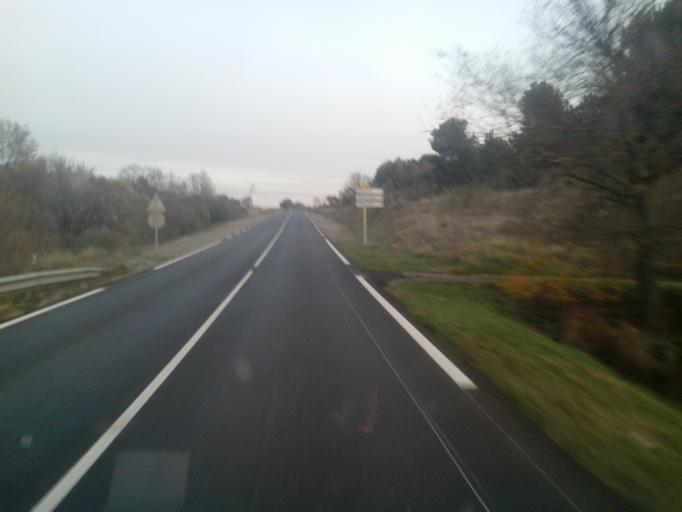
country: FR
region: Languedoc-Roussillon
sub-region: Departement de l'Aude
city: Ginestas
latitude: 43.2851
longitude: 2.8338
